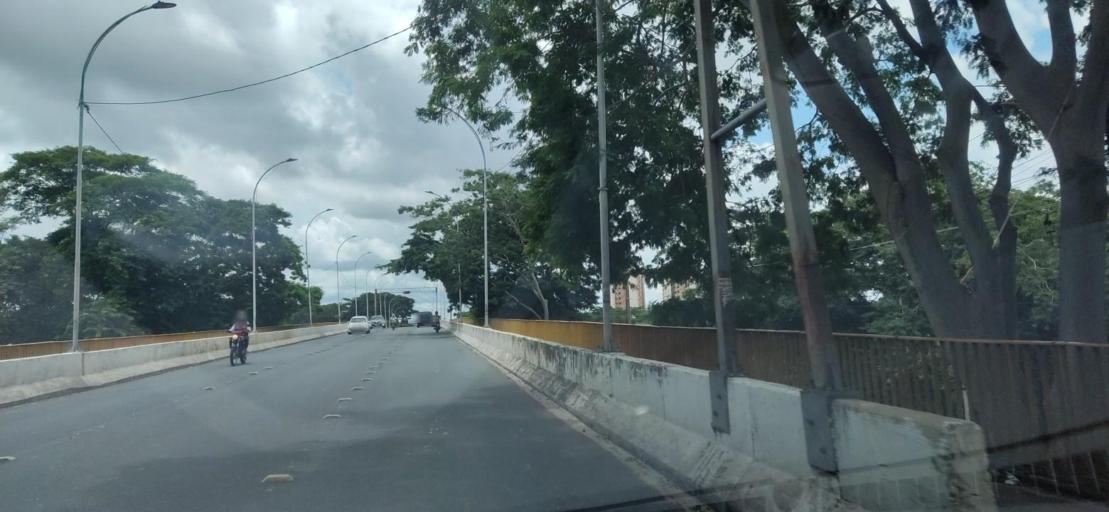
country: BR
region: Piaui
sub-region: Teresina
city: Teresina
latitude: -5.0644
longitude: -42.8083
